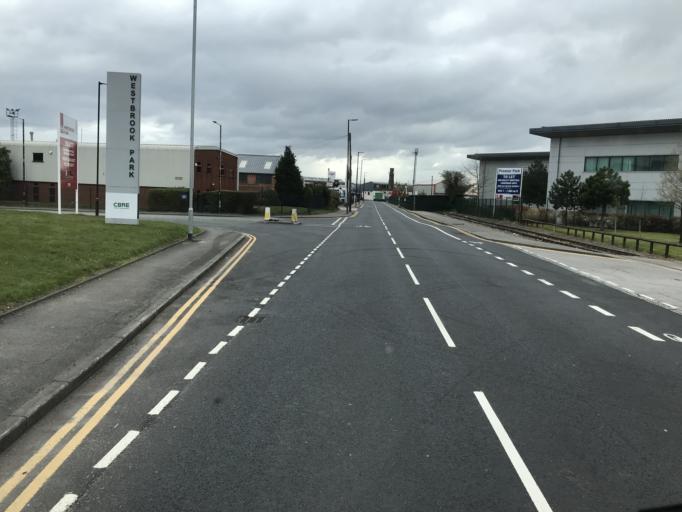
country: GB
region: England
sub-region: Trafford
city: Trafford Park
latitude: 53.4702
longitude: -2.3127
